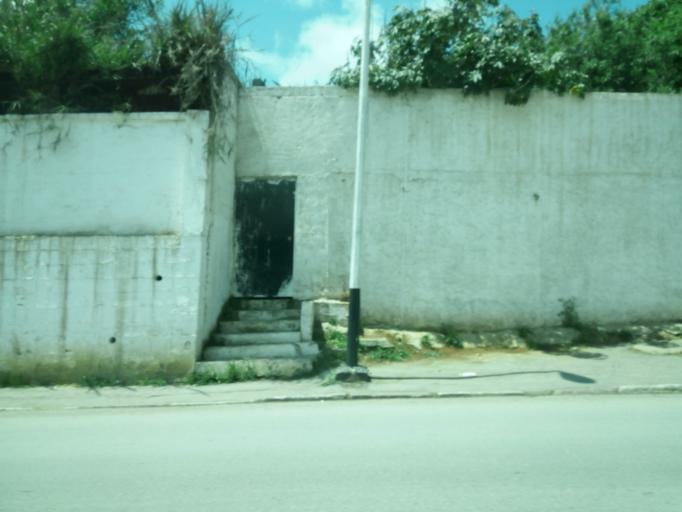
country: DZ
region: Tipaza
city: Saoula
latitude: 36.7261
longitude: 2.9903
